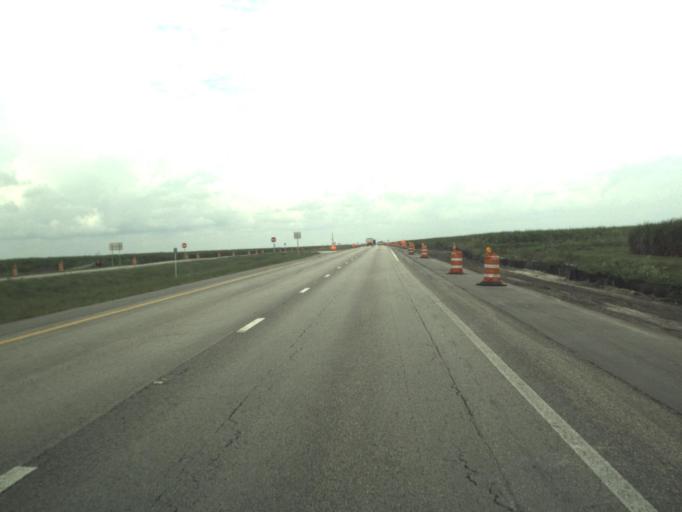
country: US
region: Florida
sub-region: Palm Beach County
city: Belle Glade
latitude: 26.7262
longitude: -80.5694
